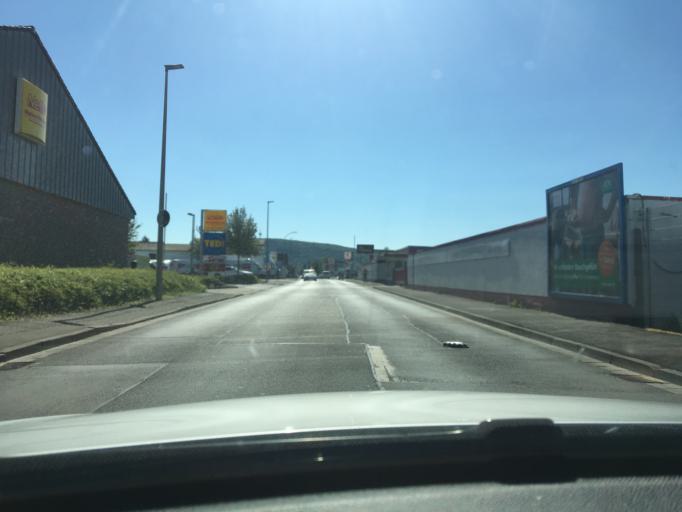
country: DE
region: Rheinland-Pfalz
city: Bad Kreuznach
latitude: 49.8476
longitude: 7.8817
